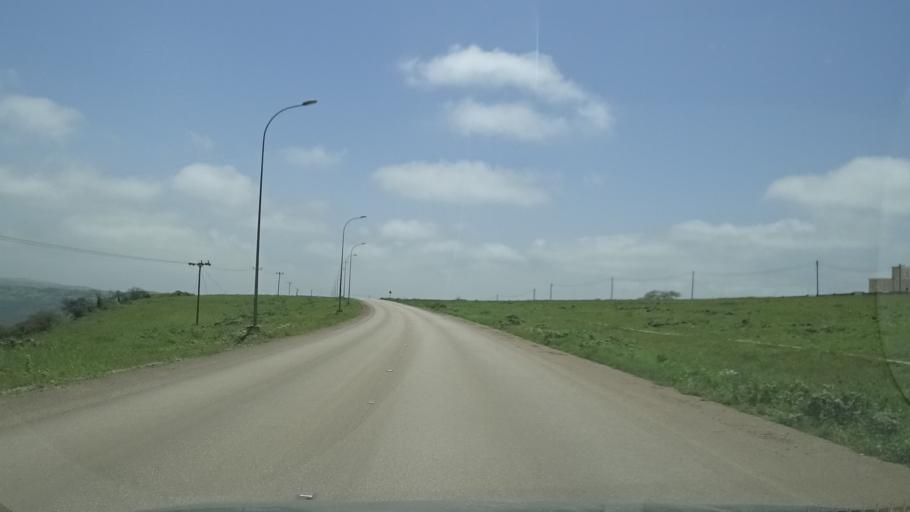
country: OM
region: Zufar
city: Salalah
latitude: 17.2305
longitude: 54.2720
